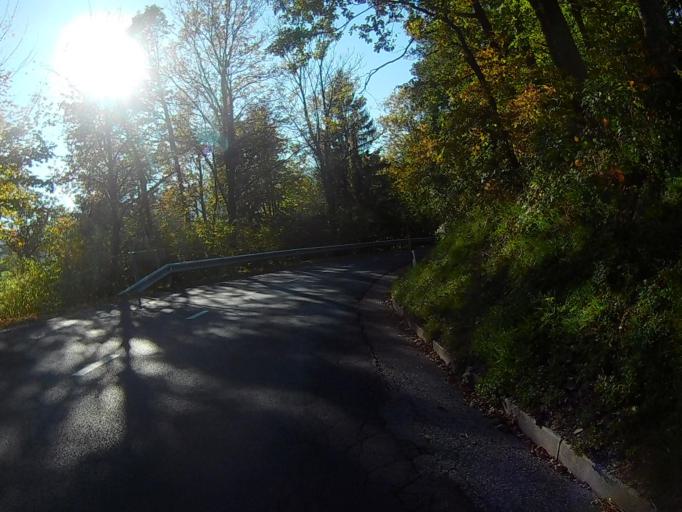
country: SI
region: Race-Fram
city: Morje
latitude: 46.4856
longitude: 15.5742
